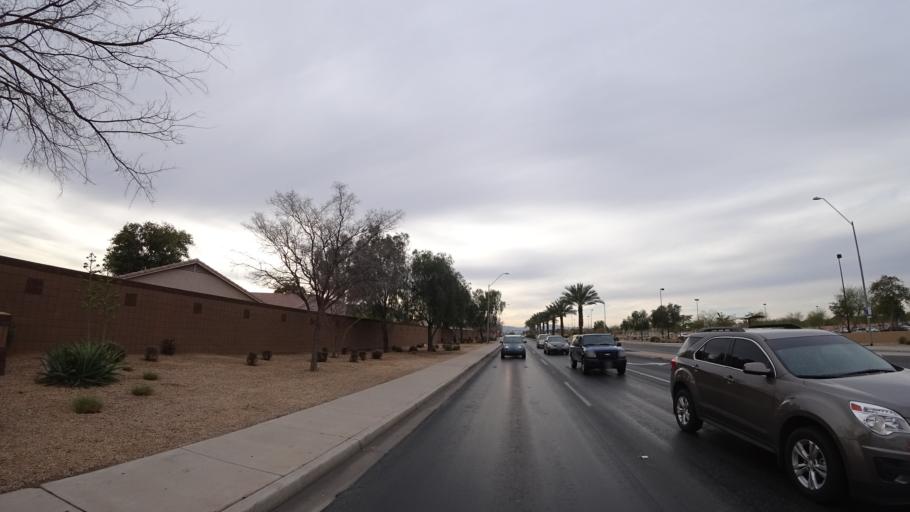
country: US
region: Arizona
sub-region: Maricopa County
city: El Mirage
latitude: 33.6090
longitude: -112.3367
